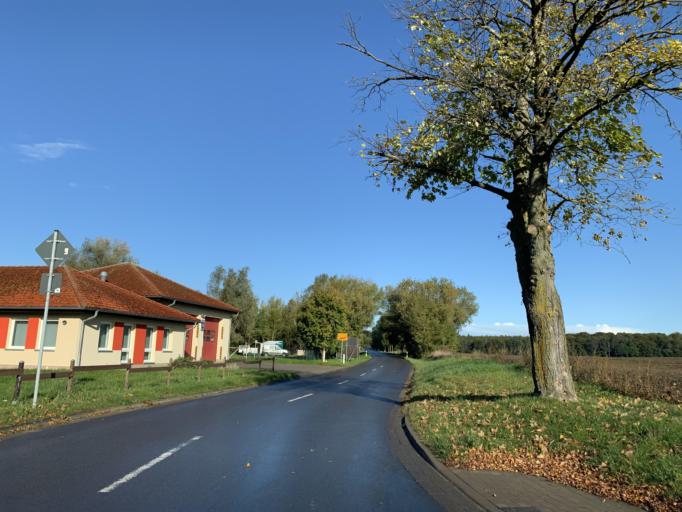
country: DE
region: Mecklenburg-Vorpommern
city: Burg Stargard
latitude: 53.4903
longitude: 13.2679
